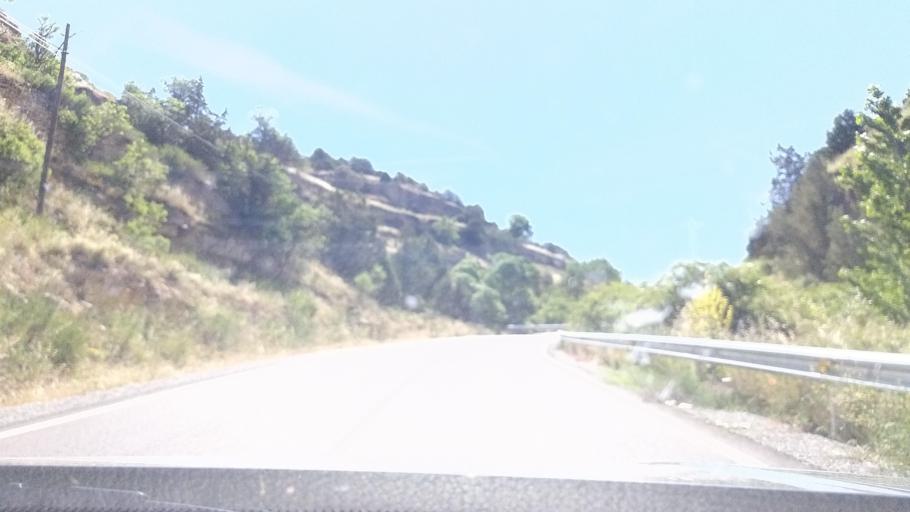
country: ES
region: Castille and Leon
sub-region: Provincia de Segovia
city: Pedraza
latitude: 41.1331
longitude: -3.8115
